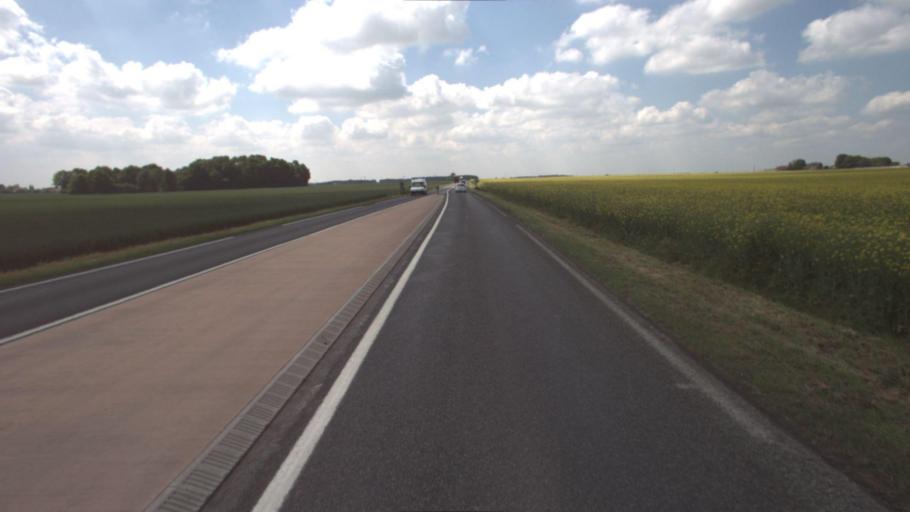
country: FR
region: Ile-de-France
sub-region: Departement de Seine-et-Marne
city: Moisenay
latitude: 48.6043
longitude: 2.7383
